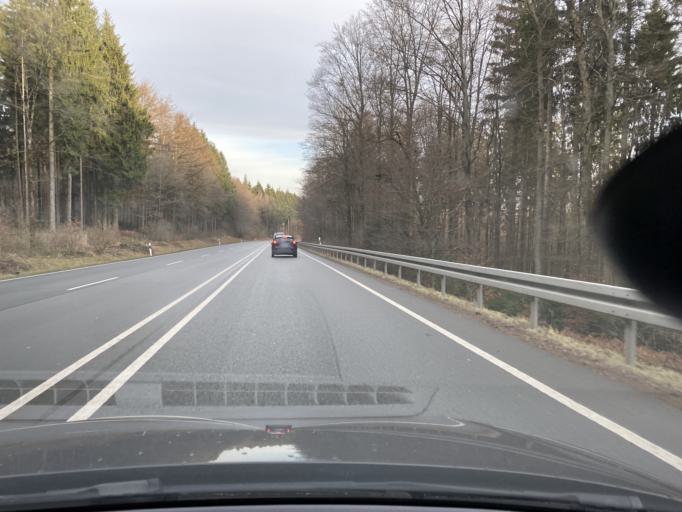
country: DE
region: North Rhine-Westphalia
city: Warstein
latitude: 51.4017
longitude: 8.3159
